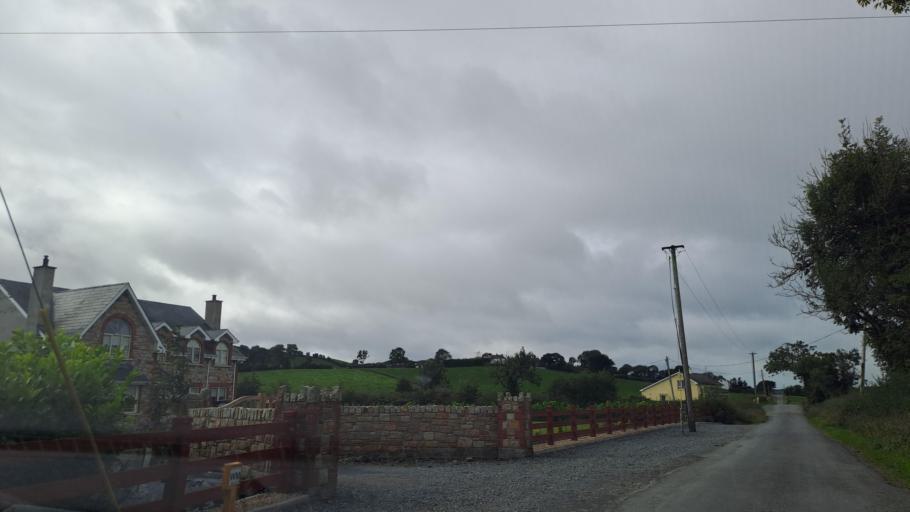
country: IE
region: Ulster
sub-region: An Cabhan
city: Bailieborough
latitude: 53.9700
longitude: -6.9001
